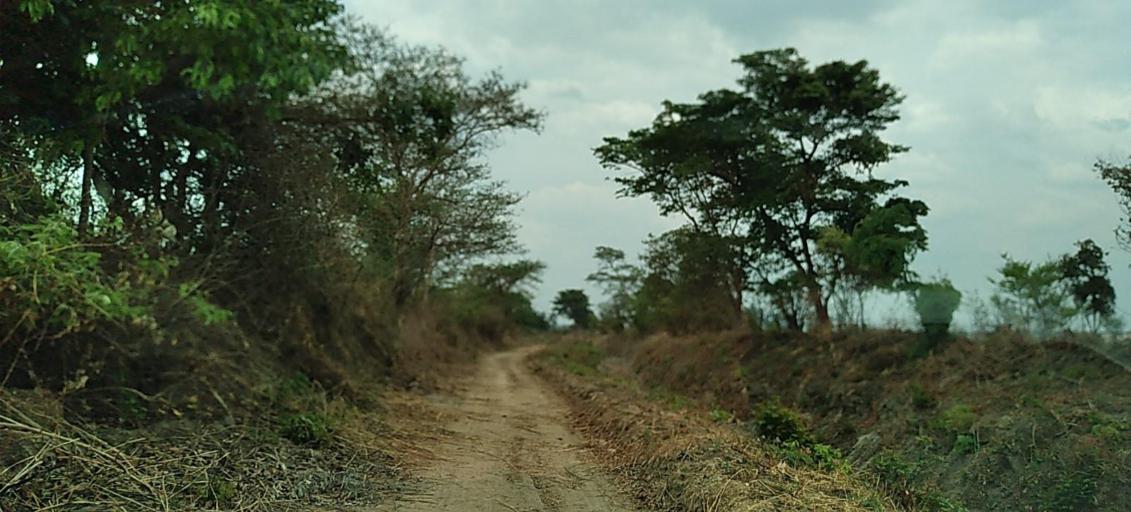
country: ZM
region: Copperbelt
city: Chililabombwe
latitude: -12.3591
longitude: 27.8032
